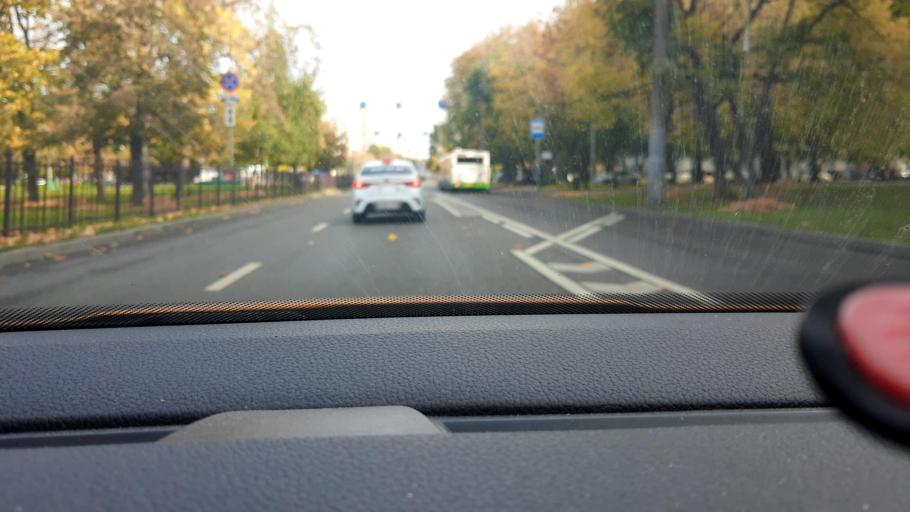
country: RU
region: Moscow
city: Kozeyevo
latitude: 55.8683
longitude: 37.6191
